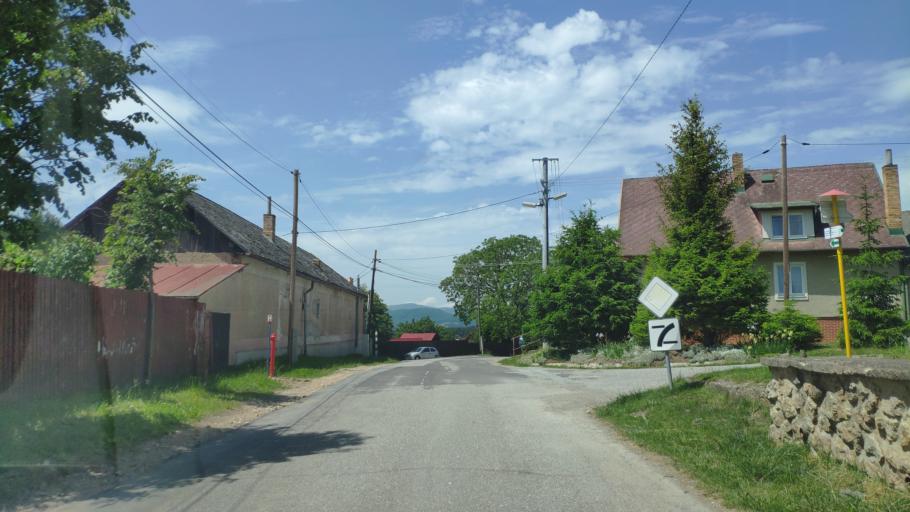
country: SK
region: Kosicky
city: Medzev
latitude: 48.7144
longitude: 20.9807
